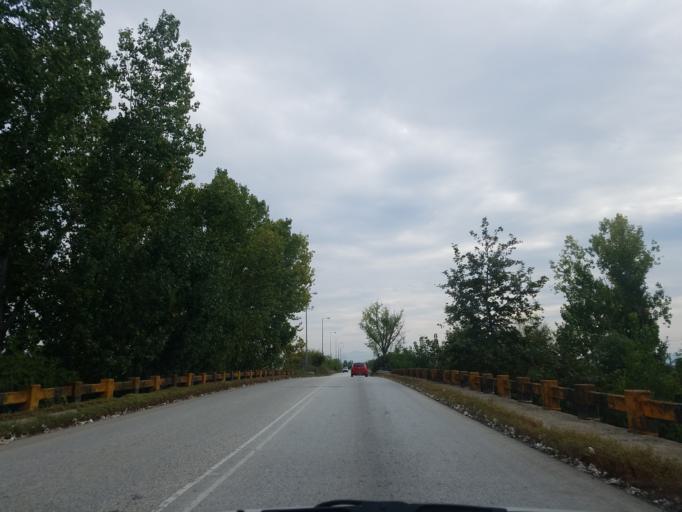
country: GR
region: Thessaly
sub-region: Nomos Kardhitsas
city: Sofades
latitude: 39.3270
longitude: 22.0941
